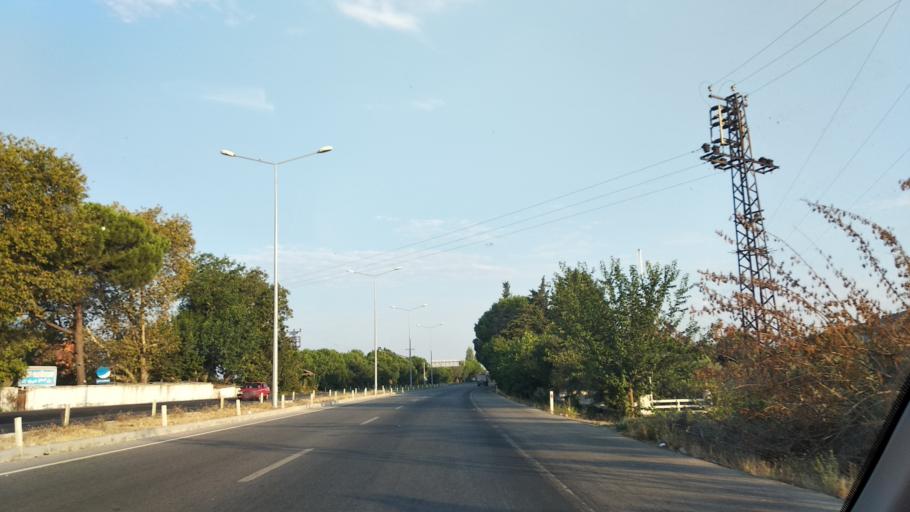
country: TR
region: Izmir
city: Dikili
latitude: 39.0808
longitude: 26.9227
